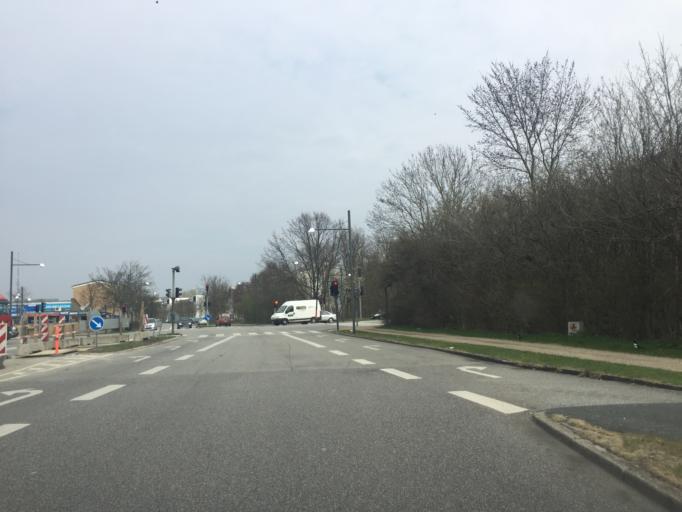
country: DK
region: Capital Region
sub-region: Kobenhavn
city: Vanlose
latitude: 55.7165
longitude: 12.4886
